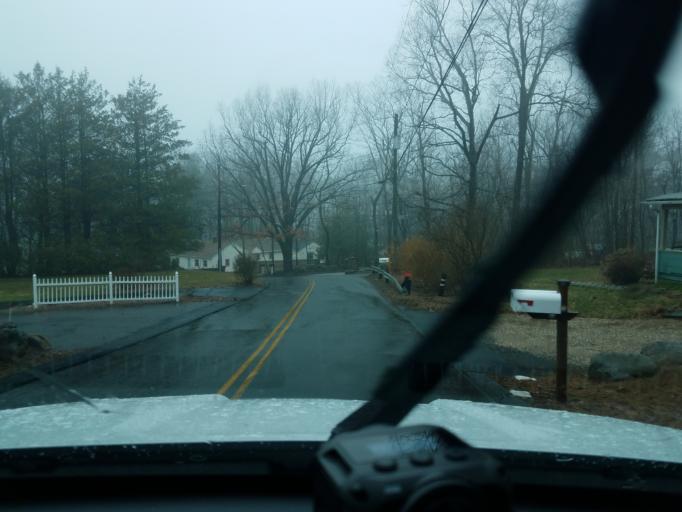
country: US
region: Connecticut
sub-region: New Haven County
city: Naugatuck
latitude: 41.5028
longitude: -73.0318
